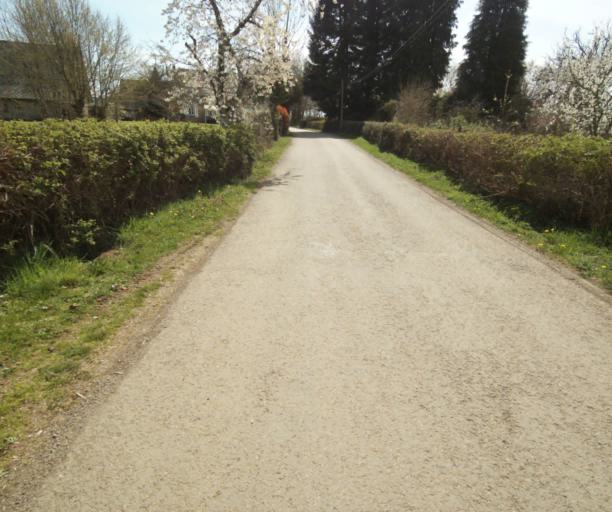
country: FR
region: Limousin
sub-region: Departement de la Correze
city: Naves
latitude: 45.3708
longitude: 1.8019
